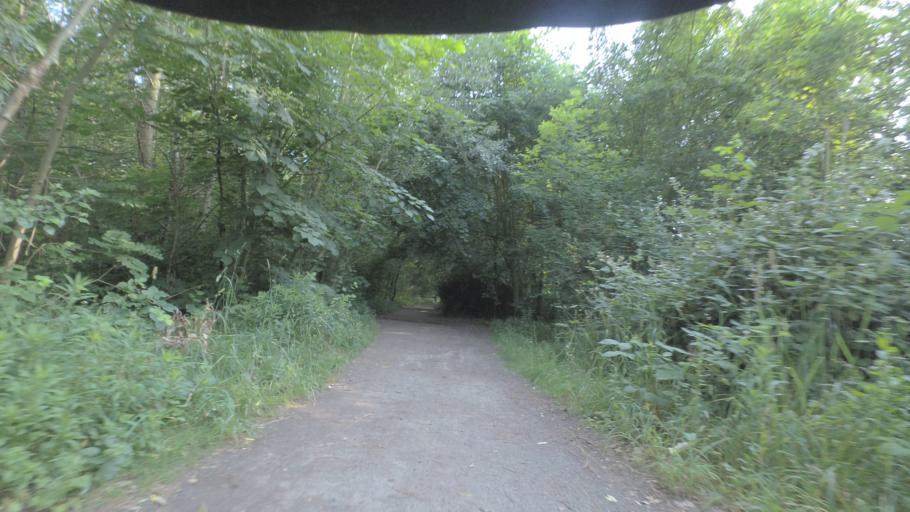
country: DE
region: Berlin
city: Lichtenrade
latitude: 52.3857
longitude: 13.4268
